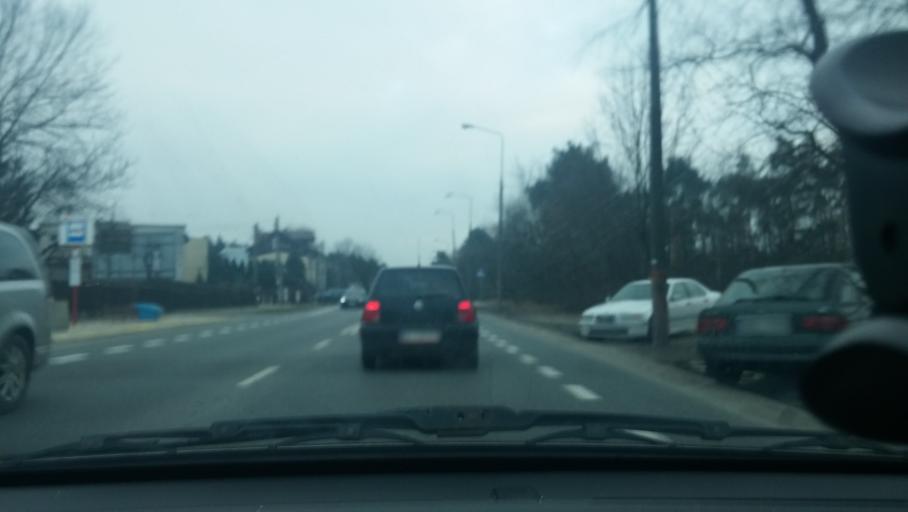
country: PL
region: Masovian Voivodeship
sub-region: Warszawa
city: Wawer
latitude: 52.2026
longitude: 21.1708
